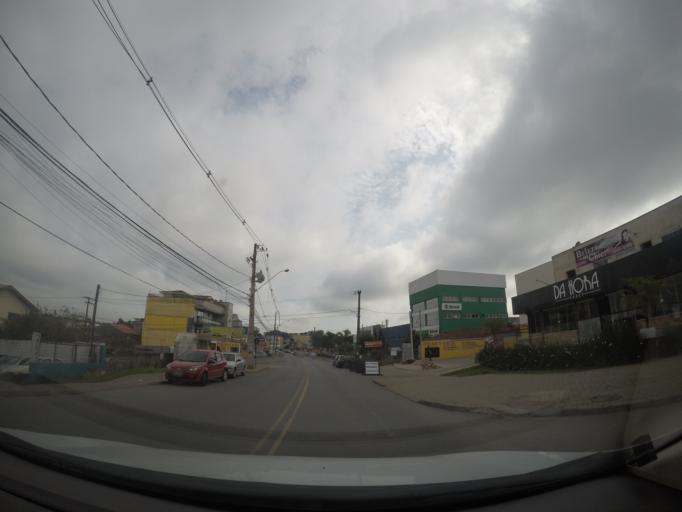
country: BR
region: Parana
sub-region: Colombo
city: Colombo
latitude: -25.3524
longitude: -49.2001
